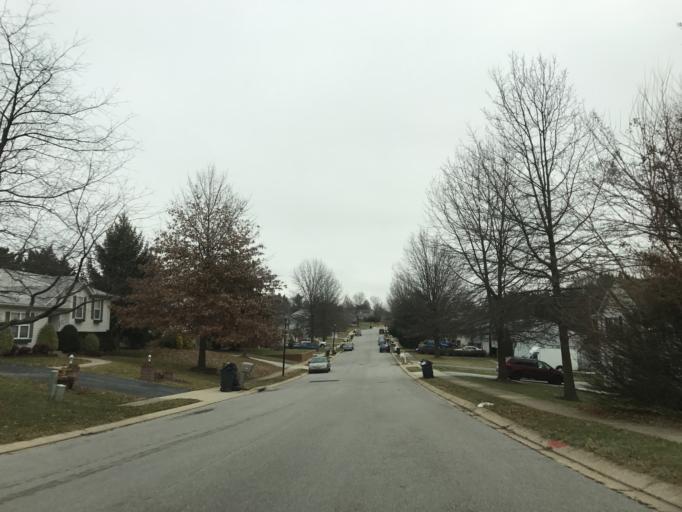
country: US
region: Maryland
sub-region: Carroll County
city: Westminster
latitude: 39.5871
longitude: -77.0217
